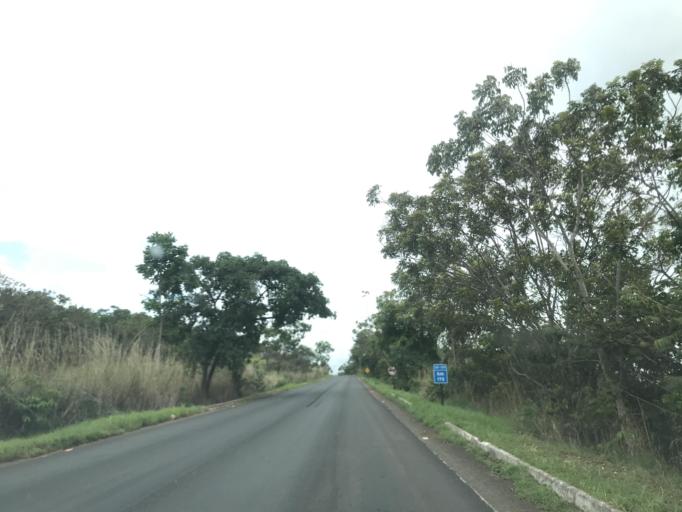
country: BR
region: Goias
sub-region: Bela Vista De Goias
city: Bela Vista de Goias
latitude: -17.0349
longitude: -48.6575
